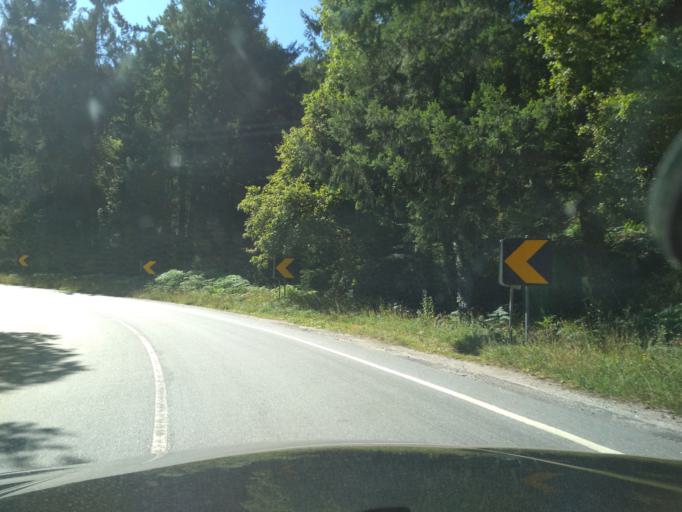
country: PT
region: Vila Real
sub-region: Ribeira de Pena
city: Ribeira de Pena
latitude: 41.5112
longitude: -7.7971
